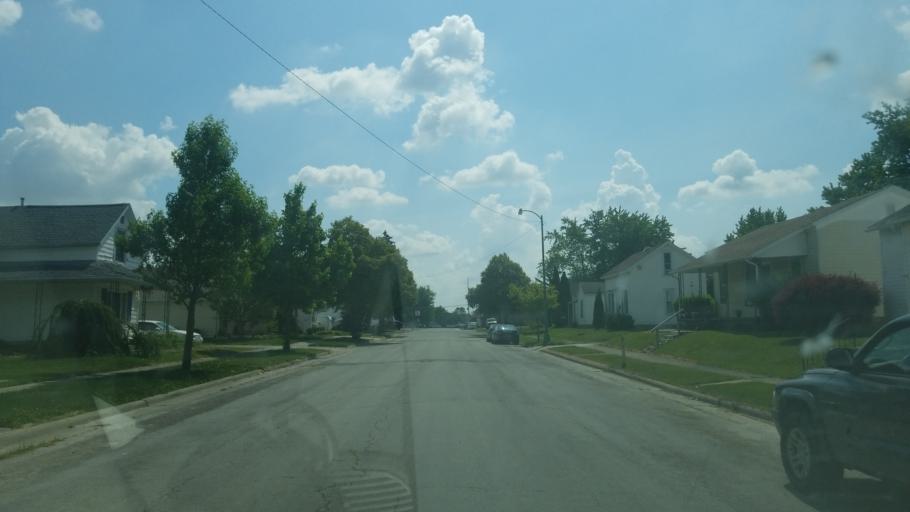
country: US
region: Ohio
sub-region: Auglaize County
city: Wapakoneta
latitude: 40.5714
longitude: -84.1858
